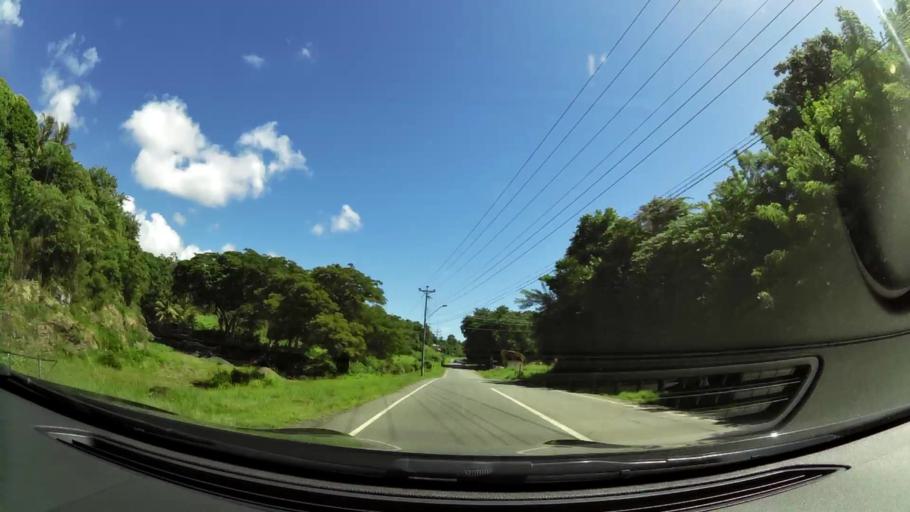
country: TT
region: Tobago
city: Scarborough
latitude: 11.1791
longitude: -60.7949
